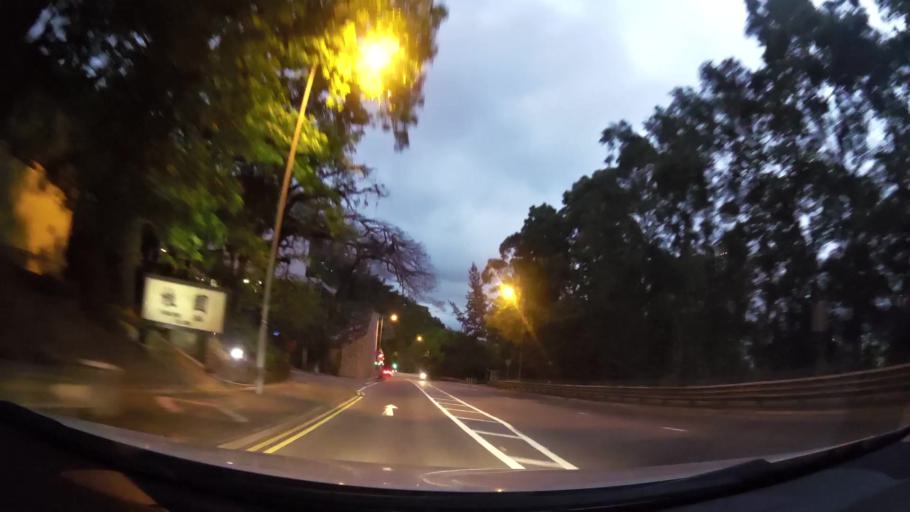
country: HK
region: Sha Tin
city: Sha Tin
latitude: 22.3678
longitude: 114.1702
